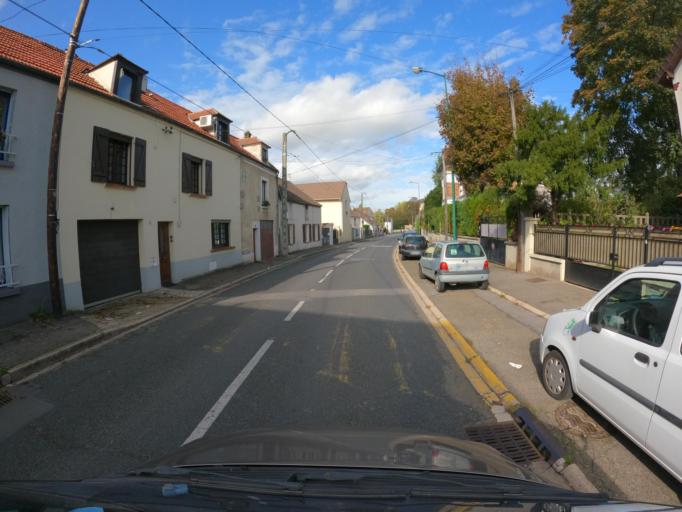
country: FR
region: Ile-de-France
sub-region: Departement de Seine-et-Marne
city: Brou-sur-Chantereine
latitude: 48.8807
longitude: 2.6340
